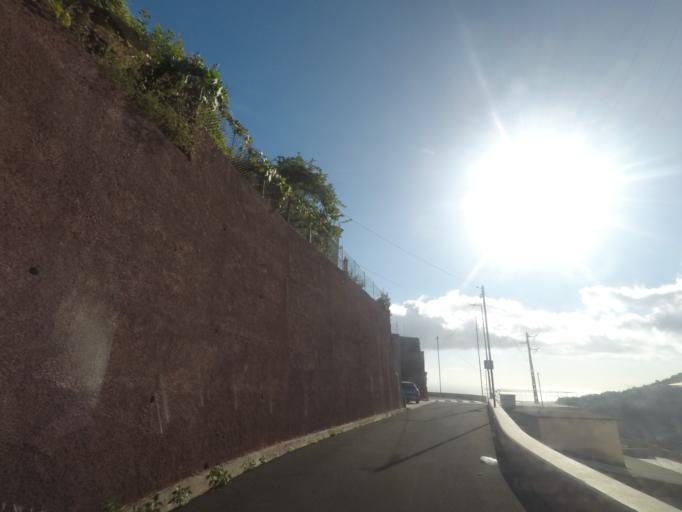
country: PT
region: Madeira
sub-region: Ribeira Brava
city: Campanario
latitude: 32.6604
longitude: -17.0070
